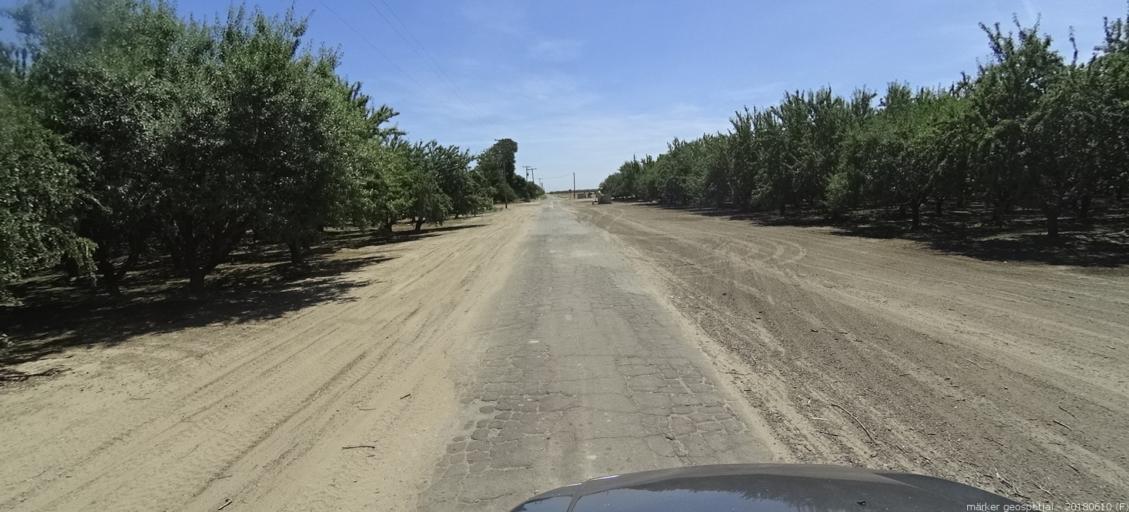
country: US
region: California
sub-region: Madera County
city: Chowchilla
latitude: 37.0470
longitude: -120.3850
